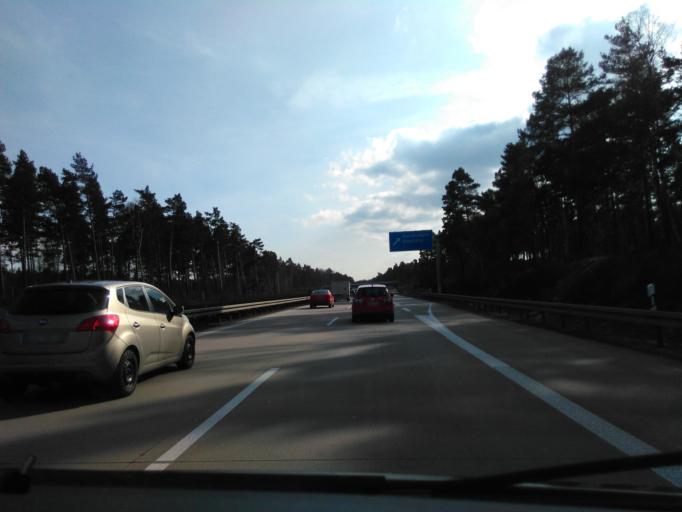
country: DE
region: Brandenburg
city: Halbe
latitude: 52.0666
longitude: 13.6520
